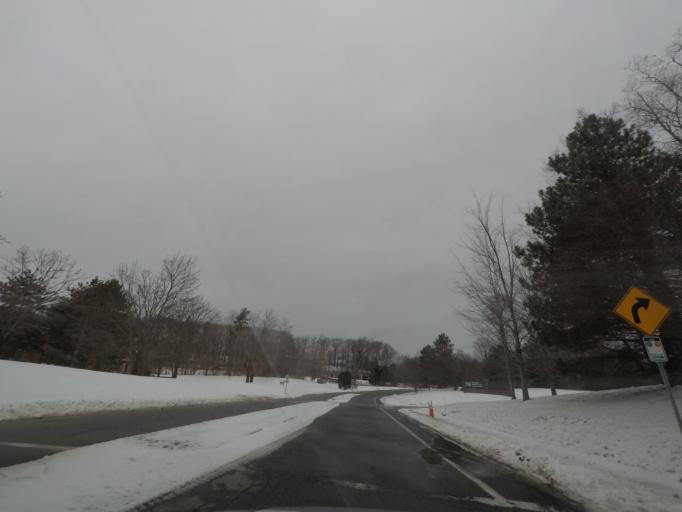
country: US
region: New York
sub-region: Schenectady County
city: Niskayuna
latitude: 42.7598
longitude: -73.8218
